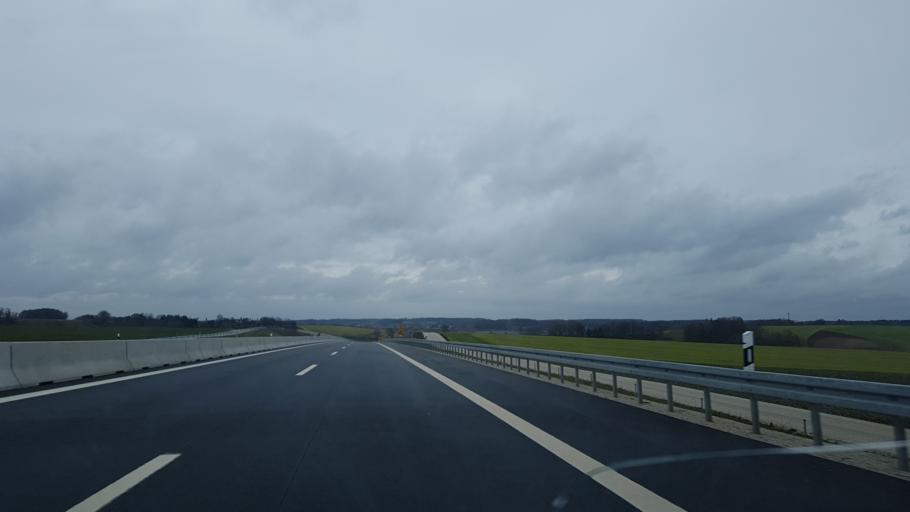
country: DE
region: Bavaria
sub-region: Lower Bavaria
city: Buch
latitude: 48.6639
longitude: 12.1884
